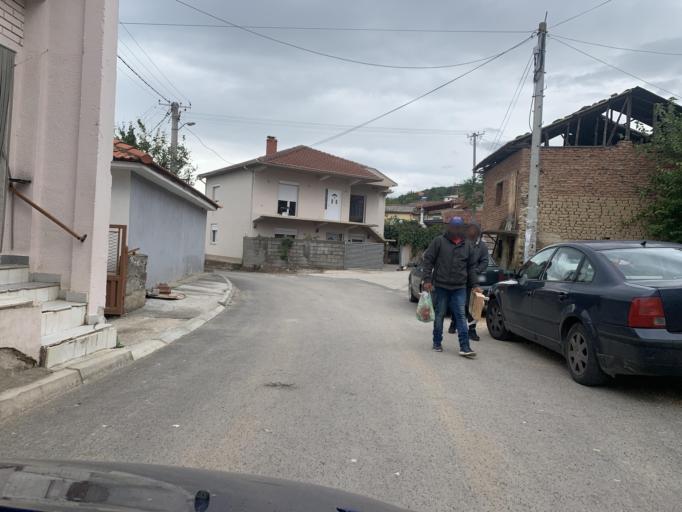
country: MK
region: Bogdanci
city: Bogdanci
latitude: 41.1934
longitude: 22.5367
